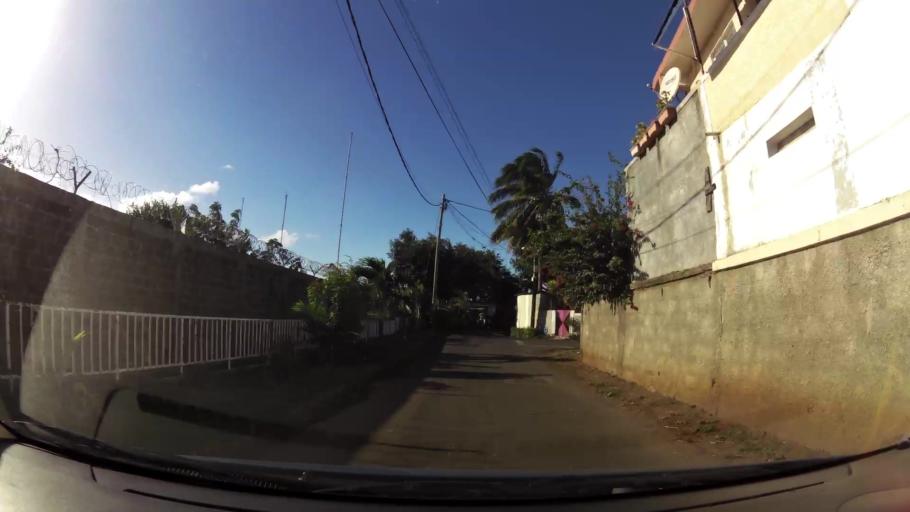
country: MU
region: Port Louis
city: Port Louis
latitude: -20.1685
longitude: 57.4781
